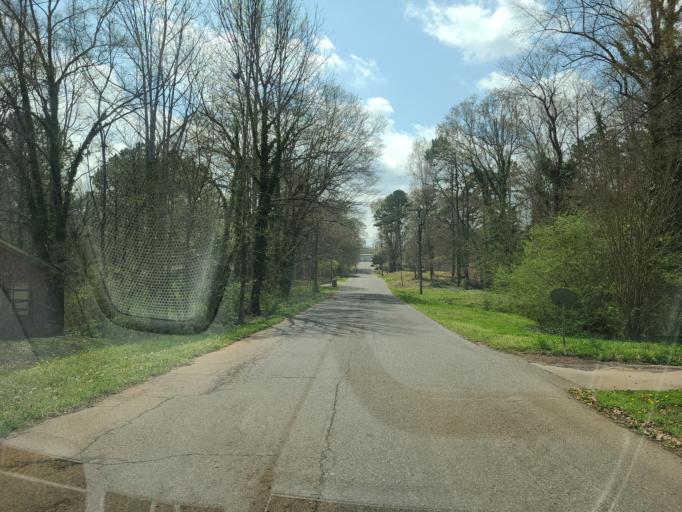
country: US
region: North Carolina
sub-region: Cleveland County
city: Shelby
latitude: 35.2736
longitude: -81.5411
